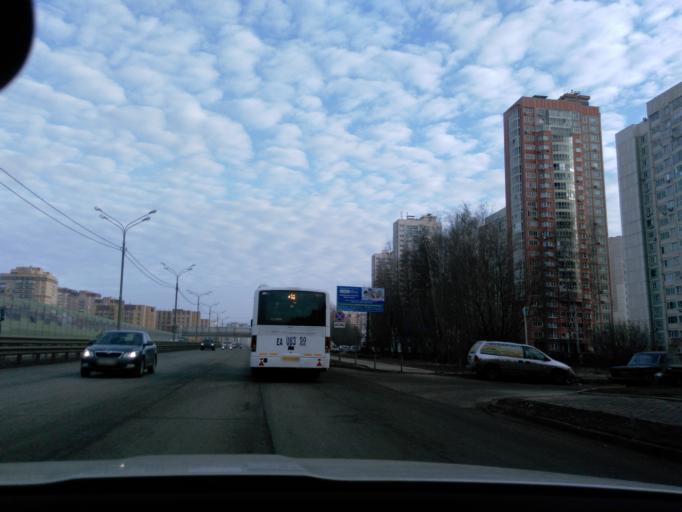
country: RU
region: Moskovskaya
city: Dolgoprudnyy
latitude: 55.9322
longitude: 37.4930
